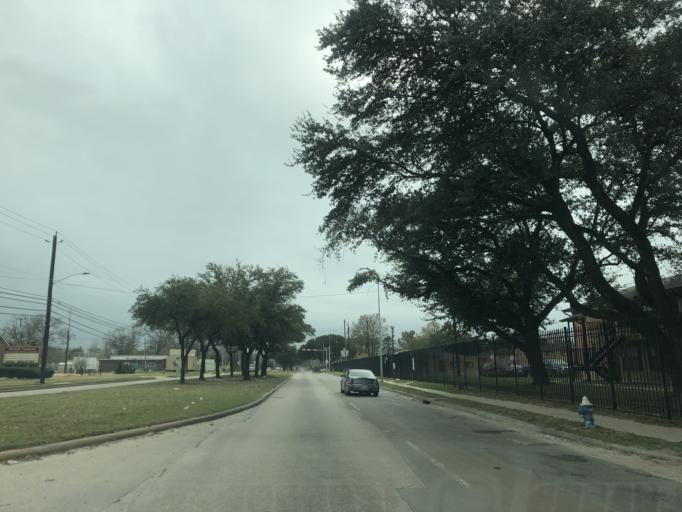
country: US
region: Texas
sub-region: Harris County
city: Jacinto City
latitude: 29.8298
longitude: -95.2845
